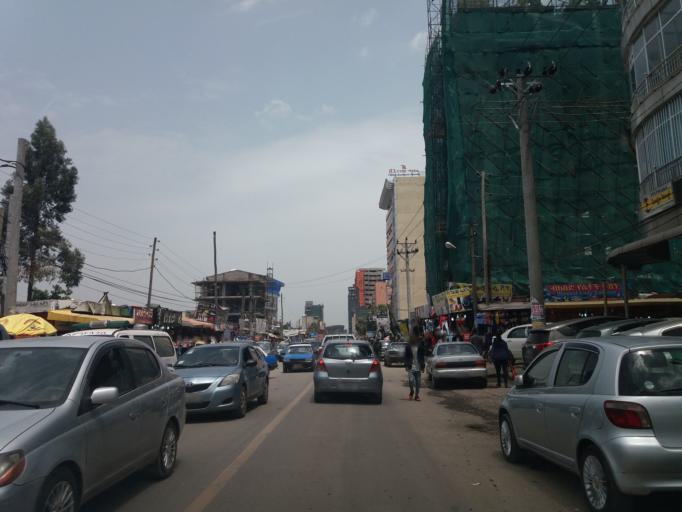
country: ET
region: Adis Abeba
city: Addis Ababa
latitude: 9.0115
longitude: 38.7879
